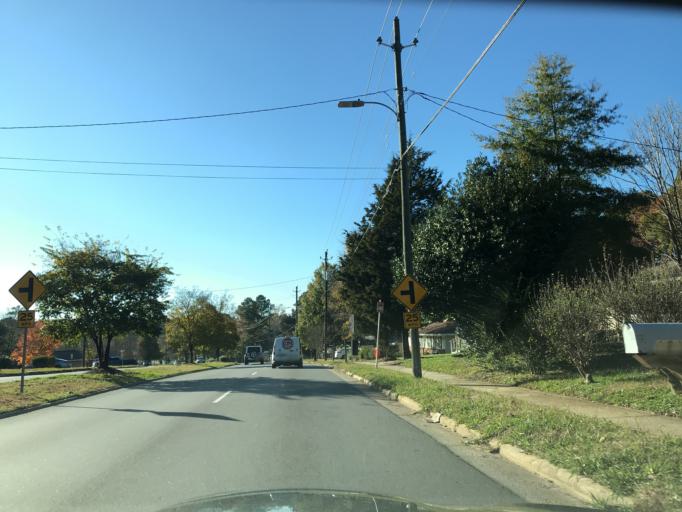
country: US
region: North Carolina
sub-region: Wake County
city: Raleigh
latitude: 35.7711
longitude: -78.6093
